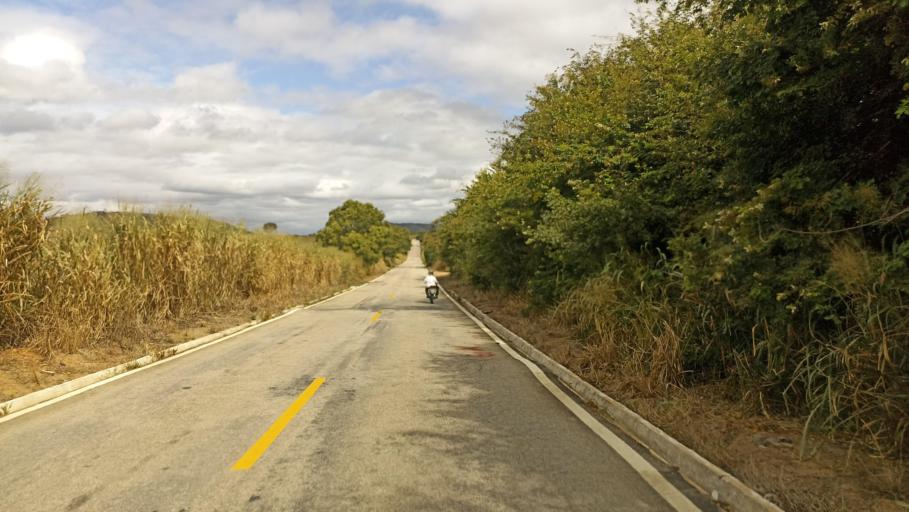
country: BR
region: Minas Gerais
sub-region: Jequitinhonha
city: Jequitinhonha
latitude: -16.5181
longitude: -41.0295
